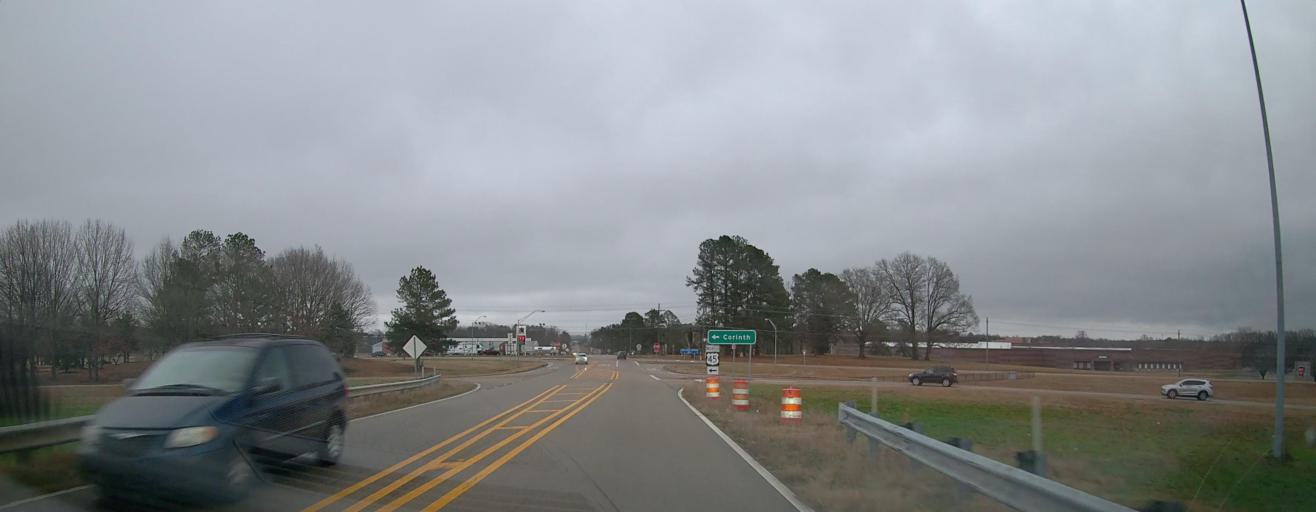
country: US
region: Mississippi
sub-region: Alcorn County
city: Corinth
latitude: 34.9091
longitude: -88.5439
